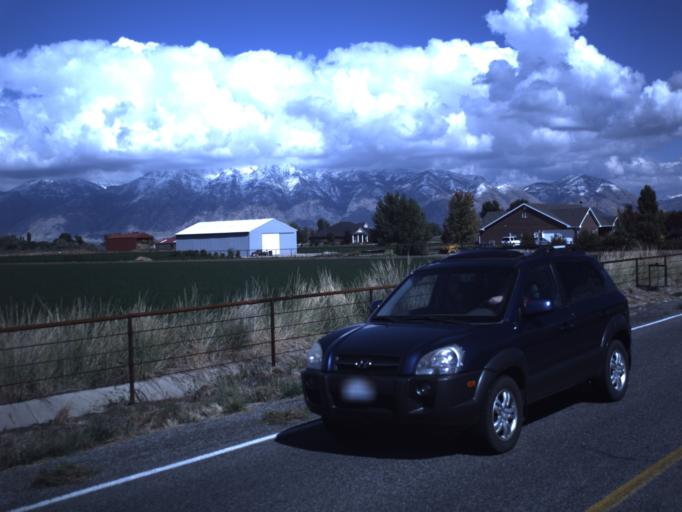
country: US
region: Utah
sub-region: Utah County
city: Benjamin
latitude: 40.1147
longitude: -111.7106
